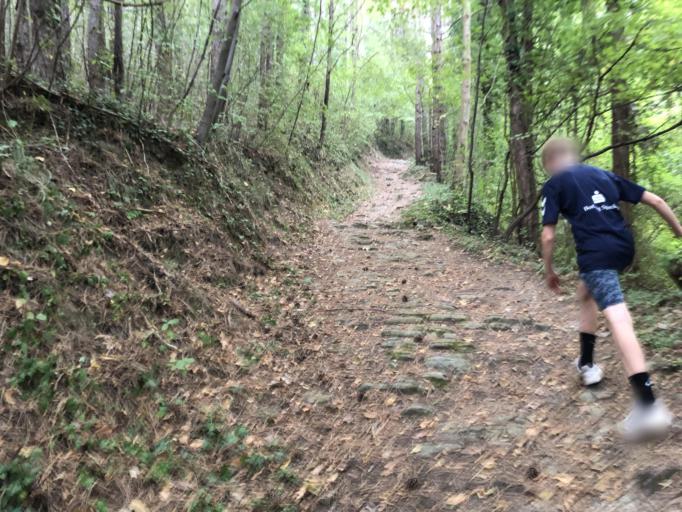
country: IT
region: Emilia-Romagna
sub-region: Forli-Cesena
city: Portico e San Benedetto
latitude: 44.0225
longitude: 11.7821
